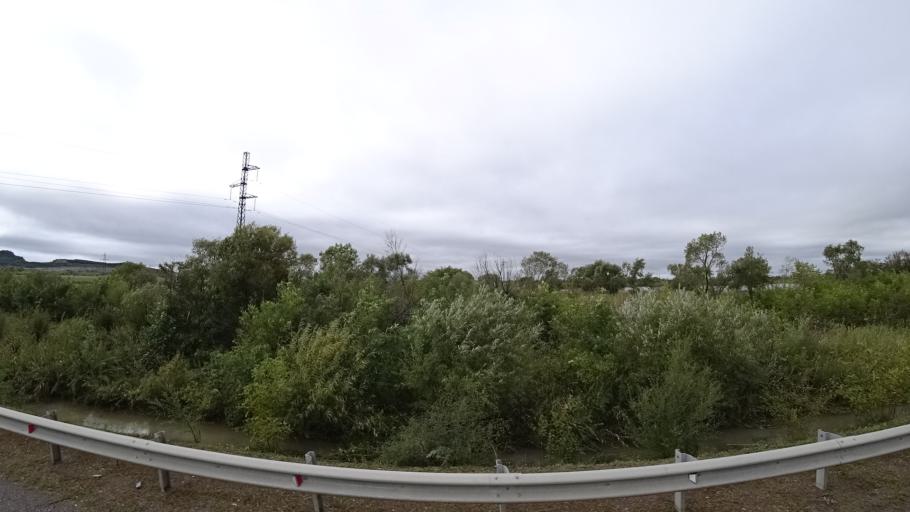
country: RU
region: Primorskiy
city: Monastyrishche
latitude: 44.1814
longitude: 132.4415
